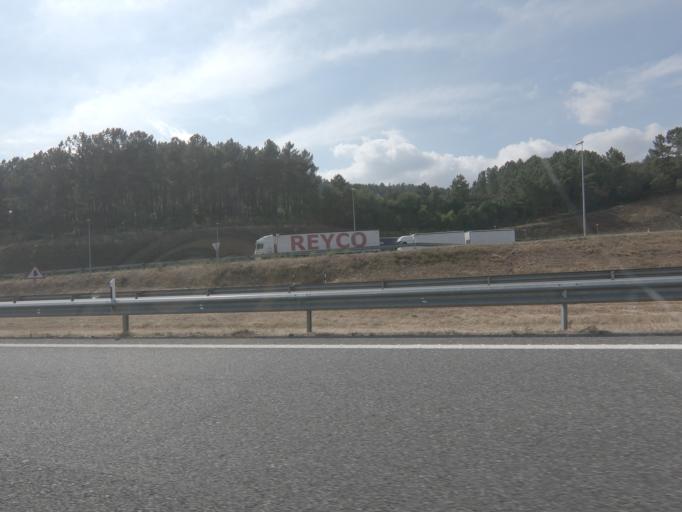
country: ES
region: Galicia
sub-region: Provincia de Ourense
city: Cenlle
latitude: 42.3132
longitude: -8.0940
